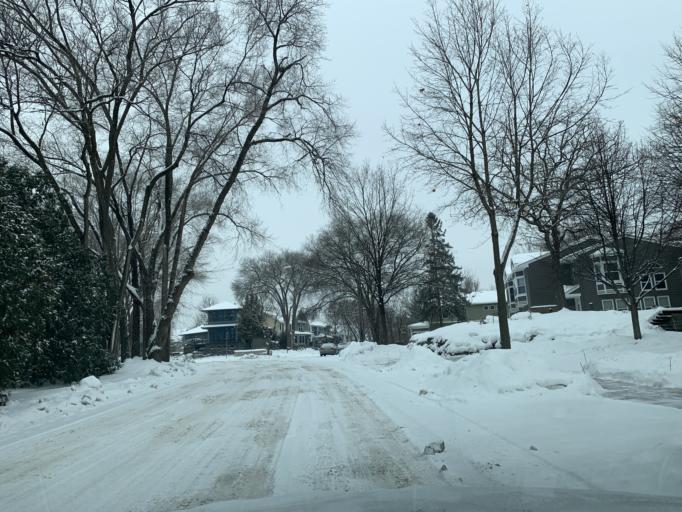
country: US
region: Minnesota
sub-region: Hennepin County
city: Saint Louis Park
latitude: 44.9523
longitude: -93.3211
